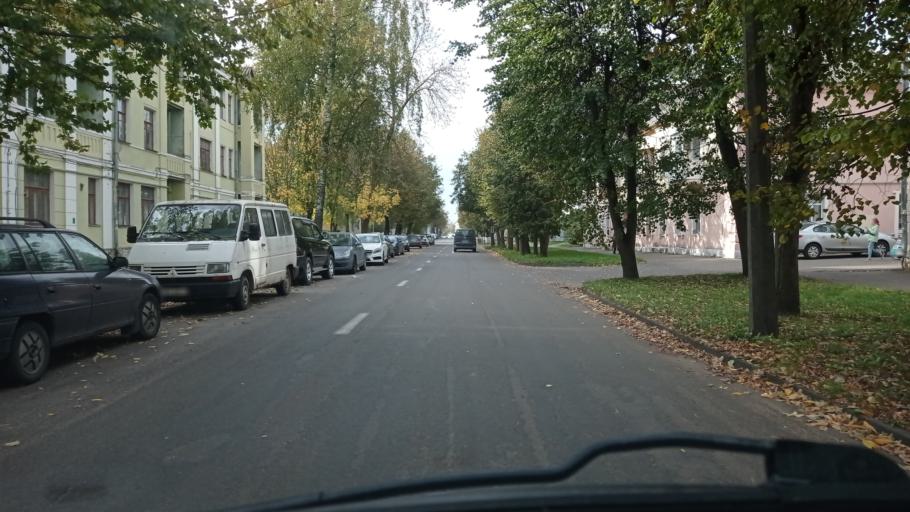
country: BY
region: Vitebsk
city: Vitebsk
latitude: 55.1834
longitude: 30.2118
